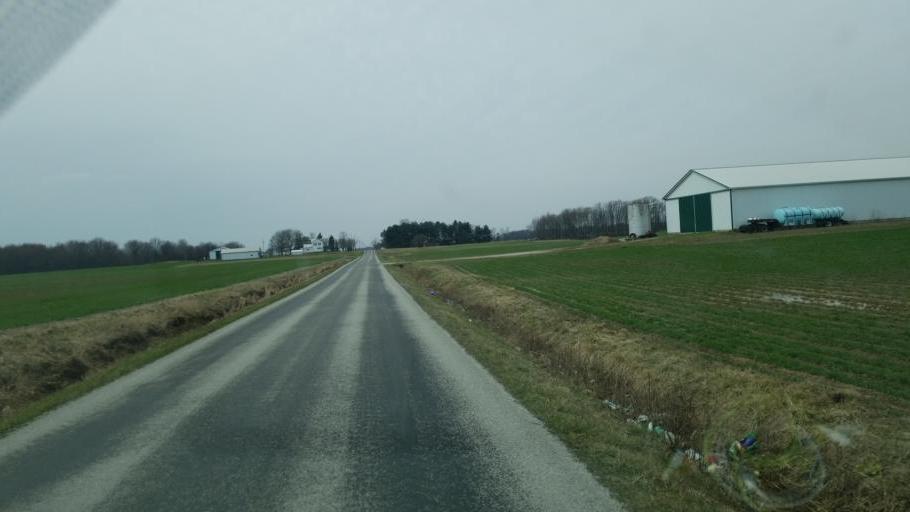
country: US
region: Ohio
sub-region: Huron County
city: Greenwich
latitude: 41.1397
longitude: -82.5493
